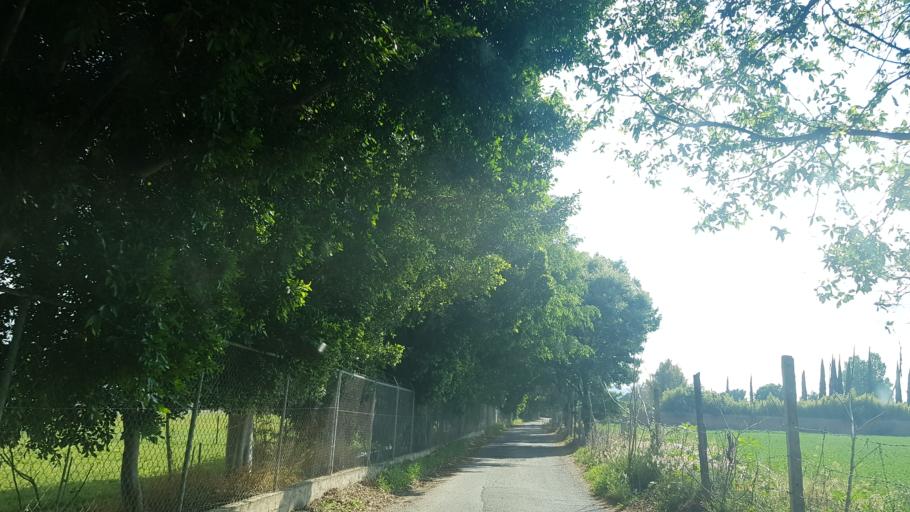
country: MX
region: Puebla
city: Atlixco
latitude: 18.8773
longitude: -98.4852
